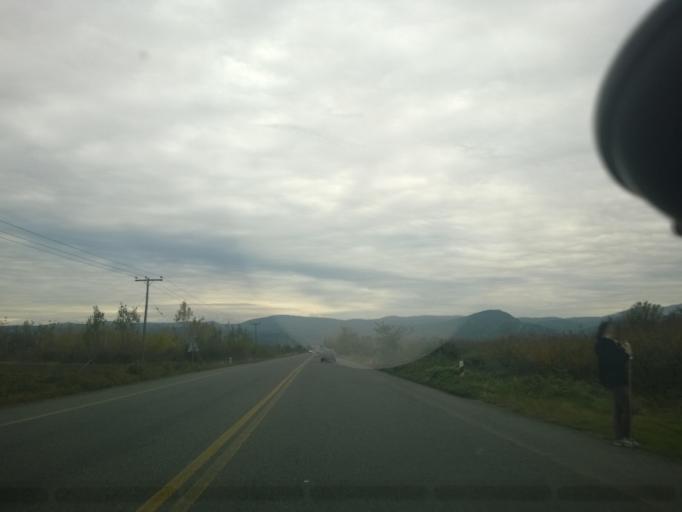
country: GR
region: Central Macedonia
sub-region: Nomos Pellis
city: Apsalos
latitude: 40.9206
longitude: 22.0793
